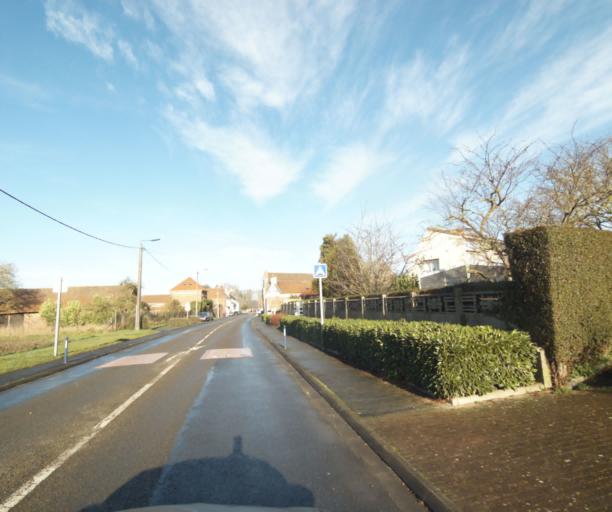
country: FR
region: Nord-Pas-de-Calais
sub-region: Departement du Nord
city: Famars
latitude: 50.3115
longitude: 3.5177
